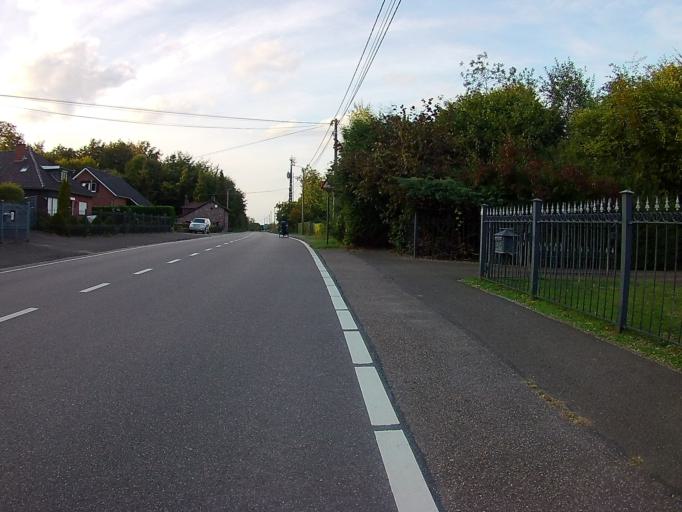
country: BE
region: Wallonia
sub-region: Province de Liege
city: Aubel
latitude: 50.7321
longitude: 5.8652
